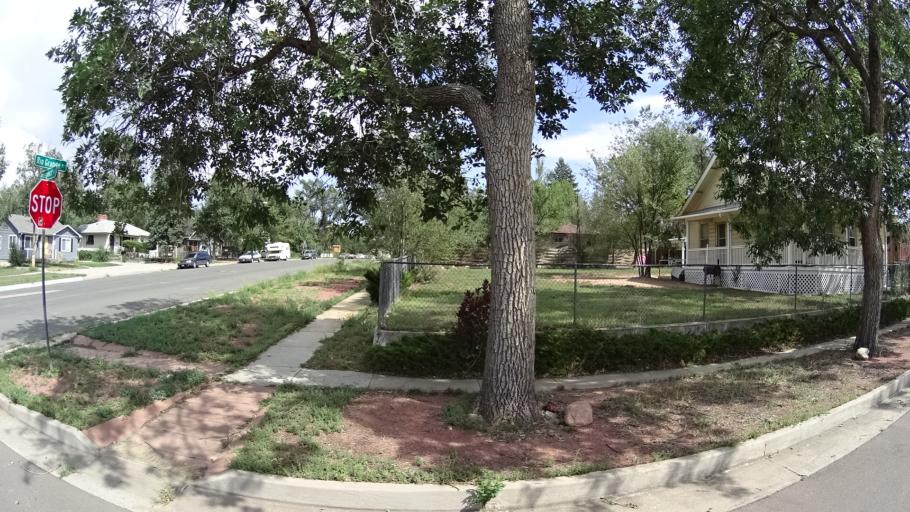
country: US
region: Colorado
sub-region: El Paso County
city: Colorado Springs
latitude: 38.8239
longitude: -104.8108
